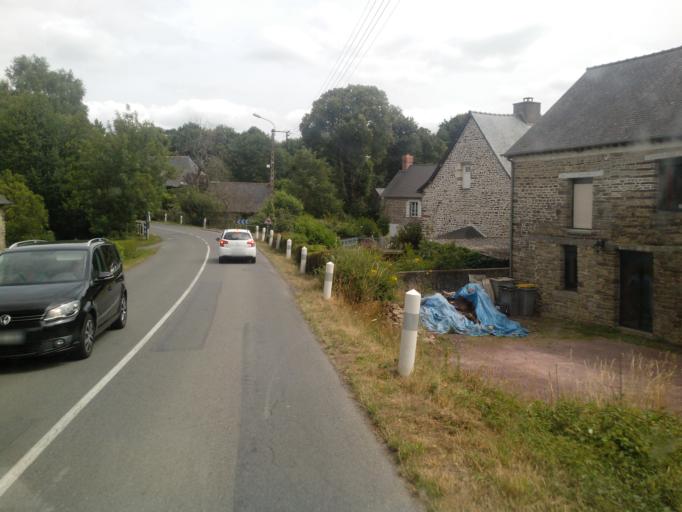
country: FR
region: Brittany
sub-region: Departement d'Ille-et-Vilaine
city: Plelan-le-Grand
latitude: 48.0023
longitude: -2.1139
